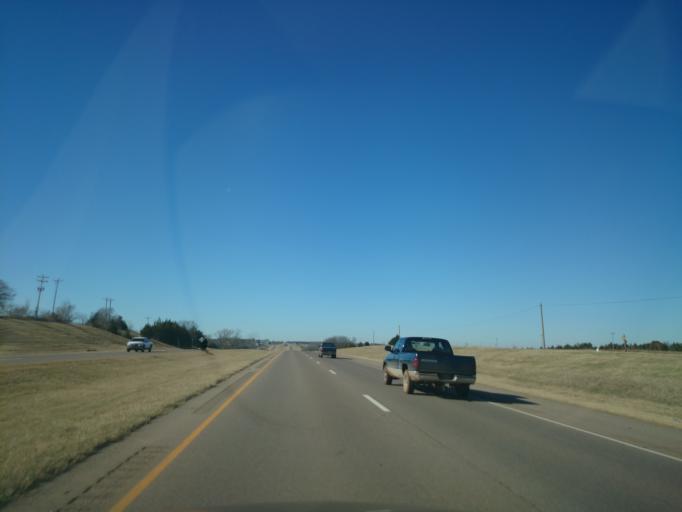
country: US
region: Oklahoma
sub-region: Payne County
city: Stillwater
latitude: 36.1161
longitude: -97.1454
